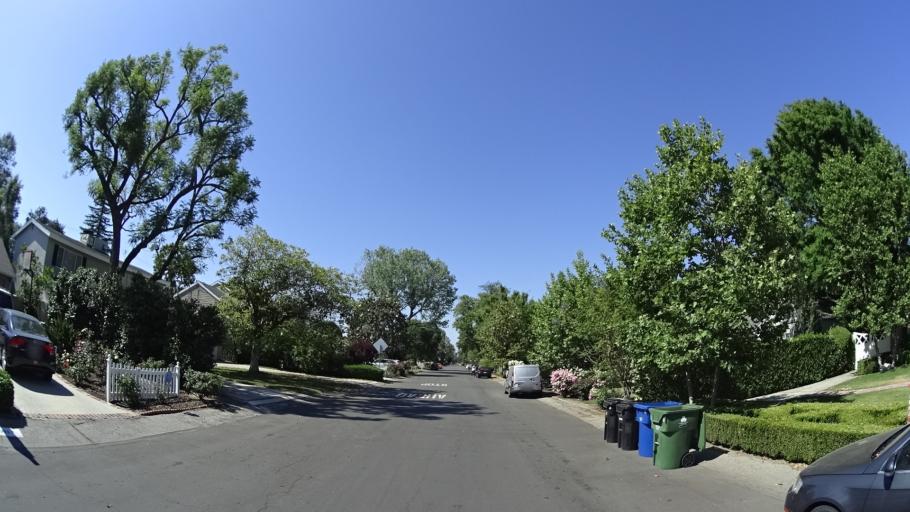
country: US
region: California
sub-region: Los Angeles County
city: North Hollywood
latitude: 34.1598
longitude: -118.3922
